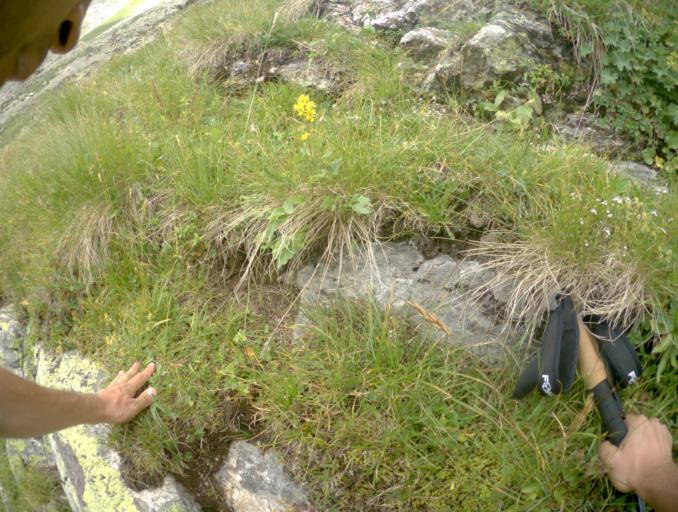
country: RU
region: Karachayevo-Cherkesiya
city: Uchkulan
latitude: 43.2852
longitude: 42.0930
